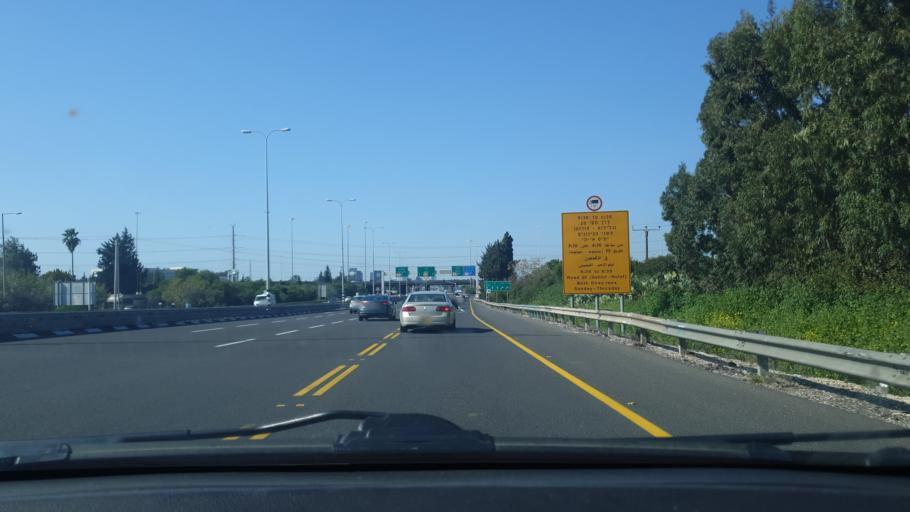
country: IL
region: Central District
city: Bet Dagan
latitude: 32.0066
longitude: 34.8173
